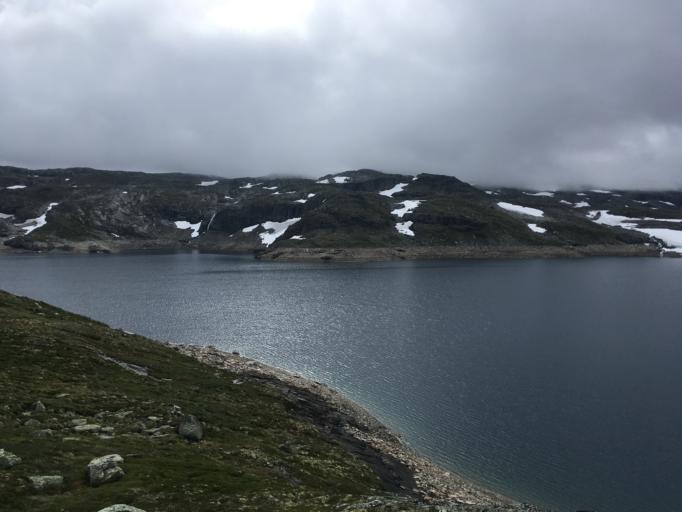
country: NO
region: Hordaland
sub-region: Odda
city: Odda
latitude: 60.0896
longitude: 6.7584
